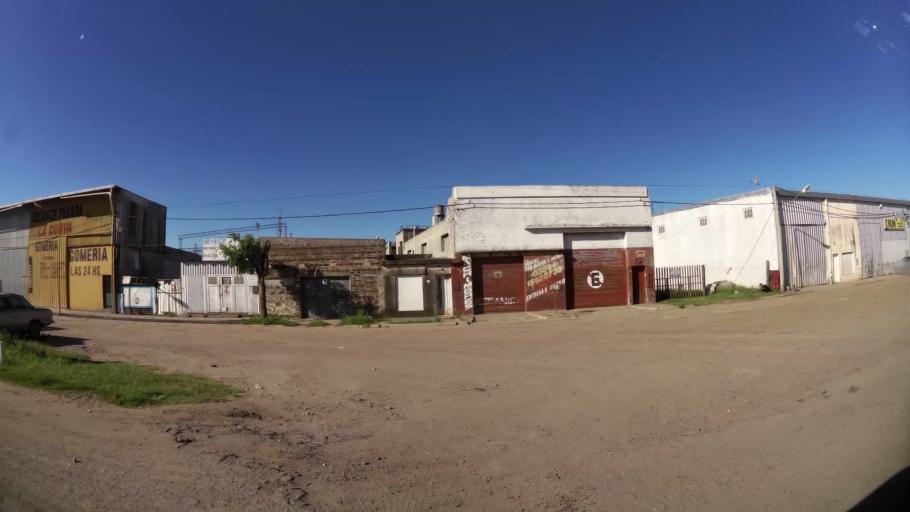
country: AR
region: Cordoba
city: San Francisco
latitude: -31.4207
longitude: -62.0603
